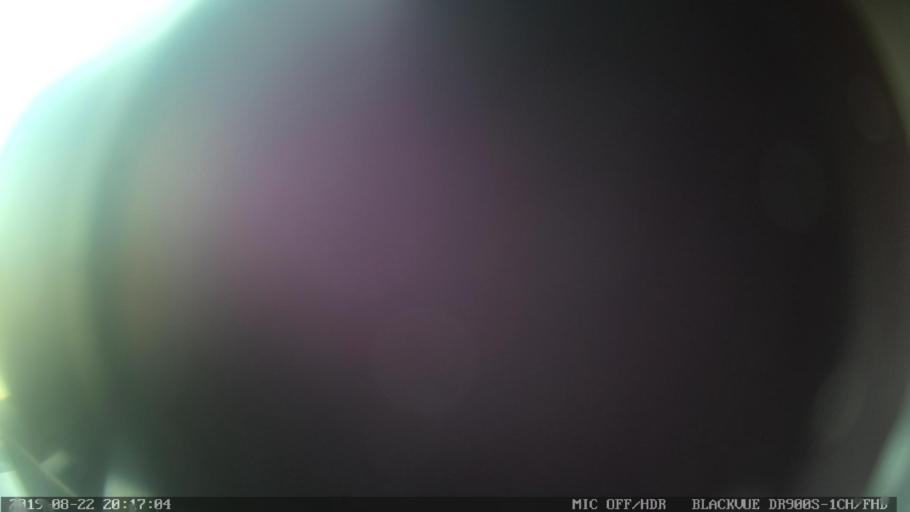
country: PT
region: Guarda
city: Alcains
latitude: 39.9240
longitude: -7.4642
